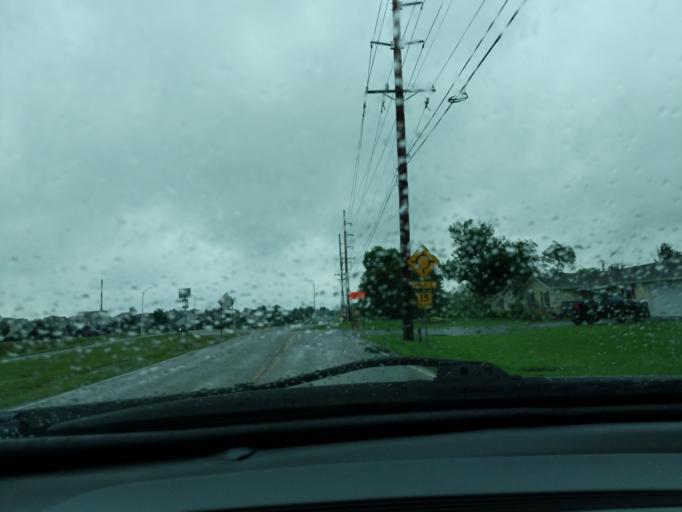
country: US
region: Indiana
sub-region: Hamilton County
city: Noblesville
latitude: 40.0736
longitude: -86.0334
